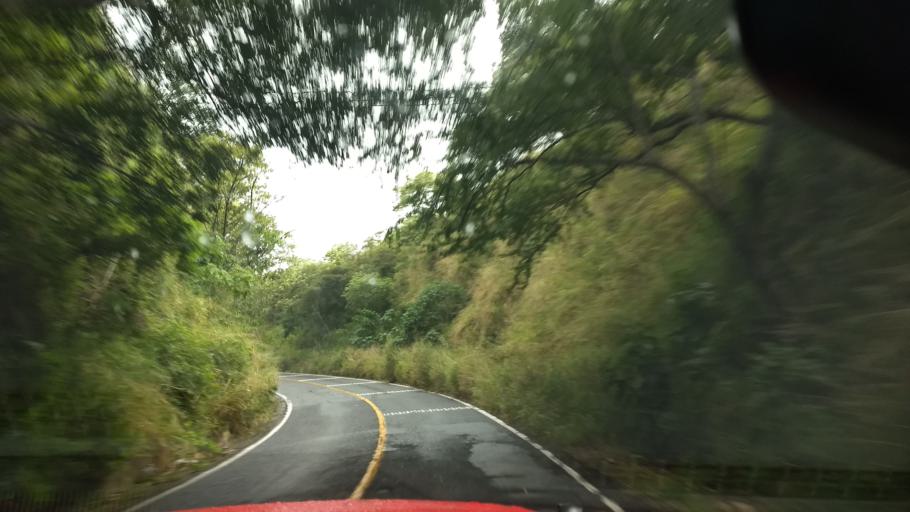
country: MX
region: Jalisco
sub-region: Tonila
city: San Marcos
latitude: 19.4359
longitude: -103.4949
